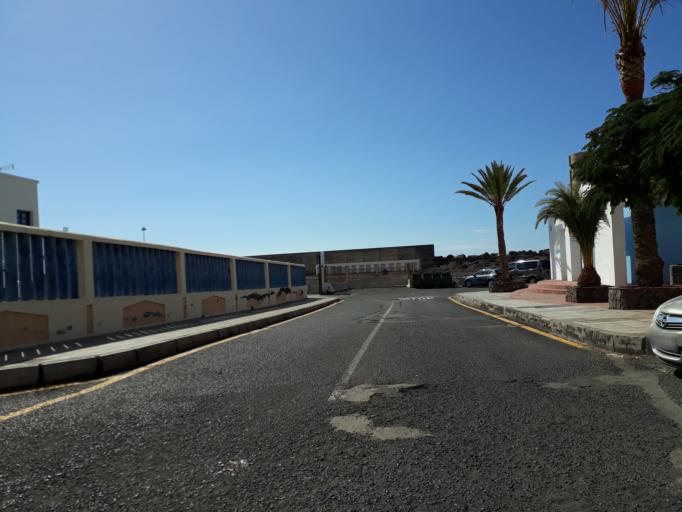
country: ES
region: Canary Islands
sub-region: Provincia de Santa Cruz de Tenerife
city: Alajero
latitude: 28.0822
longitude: -17.3337
